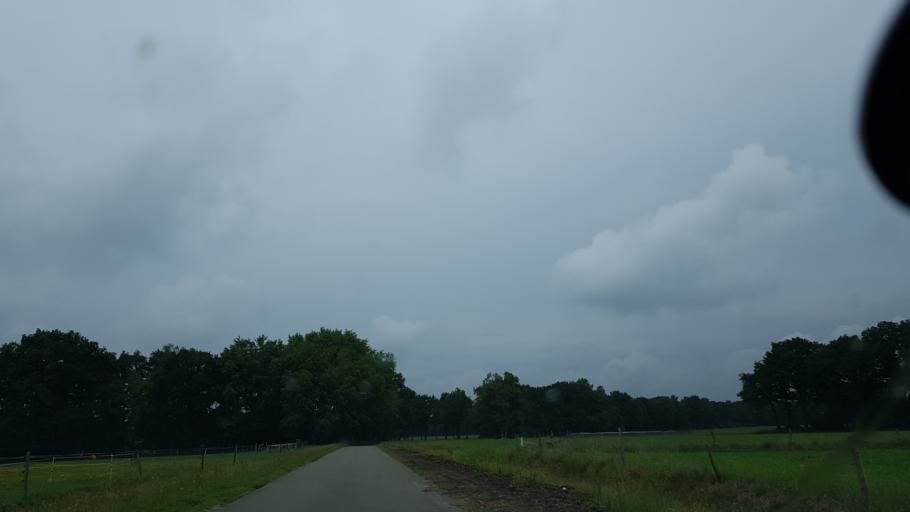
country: NL
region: Drenthe
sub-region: Gemeente Assen
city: Assen
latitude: 53.0266
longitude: 6.6046
